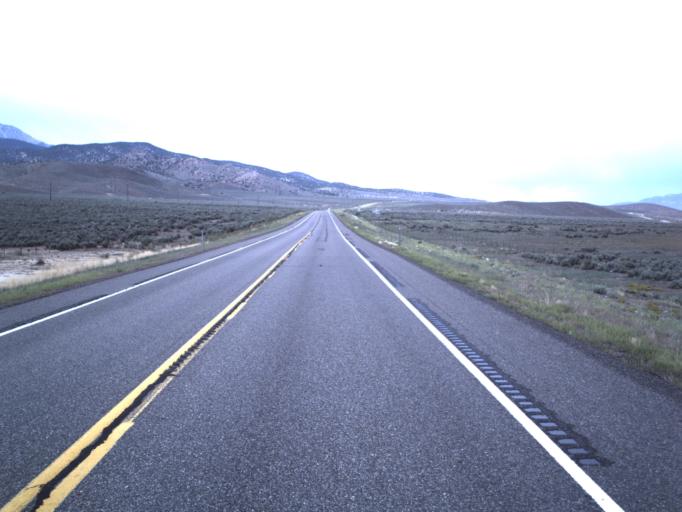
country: US
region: Utah
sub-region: Piute County
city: Junction
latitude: 38.2765
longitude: -112.2236
